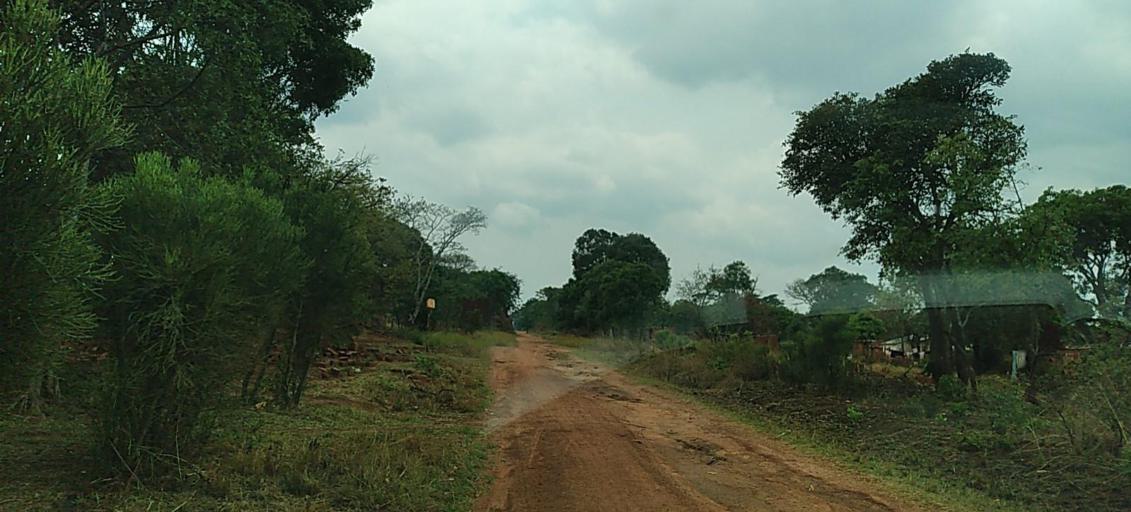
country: ZM
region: North-Western
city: Mwinilunga
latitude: -11.5304
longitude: 24.7851
